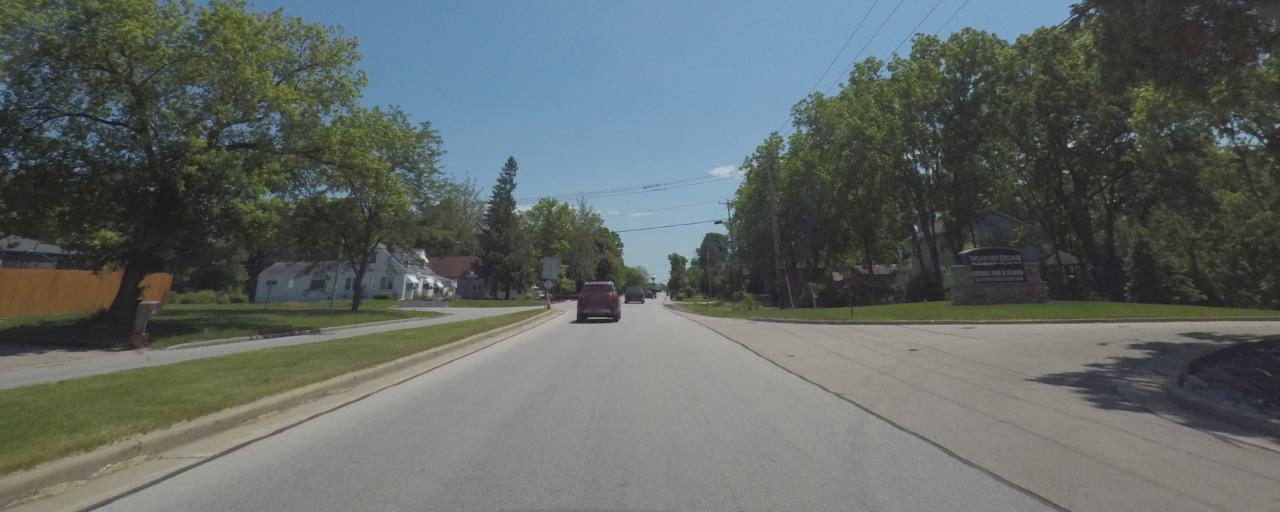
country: US
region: Wisconsin
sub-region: Waukesha County
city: New Berlin
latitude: 43.0156
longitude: -88.1271
